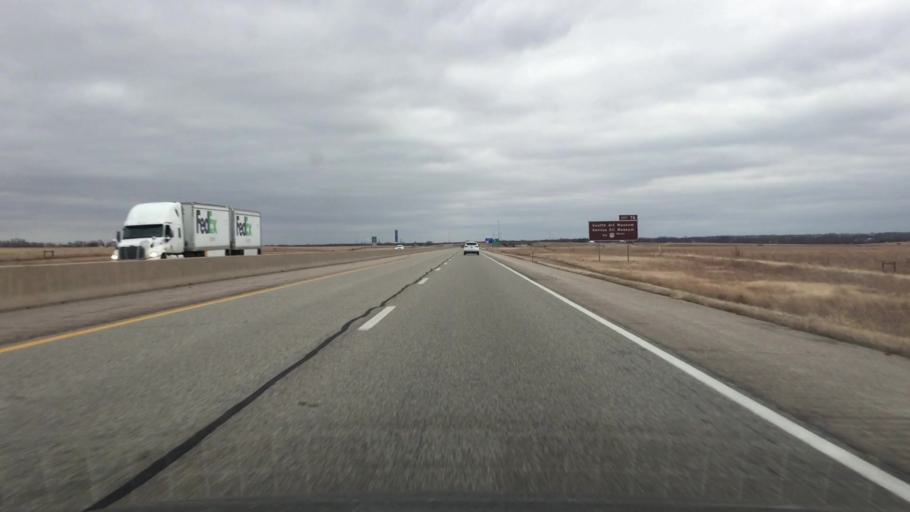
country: US
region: Kansas
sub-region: Butler County
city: El Dorado
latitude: 37.8861
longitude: -96.8401
